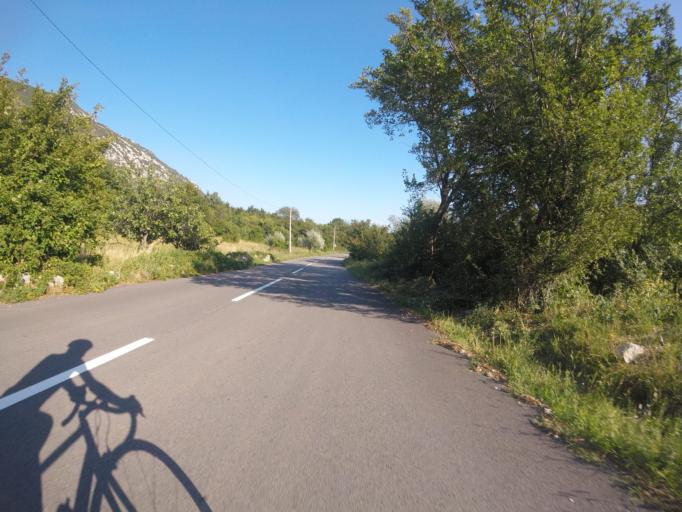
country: HR
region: Primorsko-Goranska
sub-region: Grad Crikvenica
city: Jadranovo
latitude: 45.2533
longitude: 14.6235
